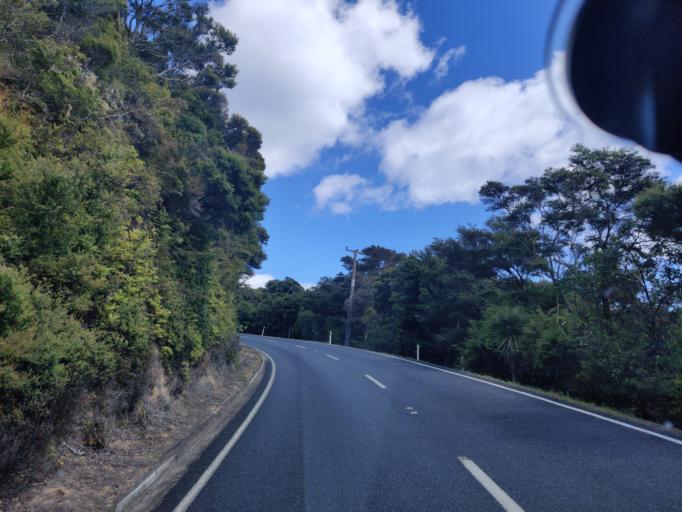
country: NZ
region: Northland
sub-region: Far North District
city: Paihia
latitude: -35.2621
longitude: 174.2607
